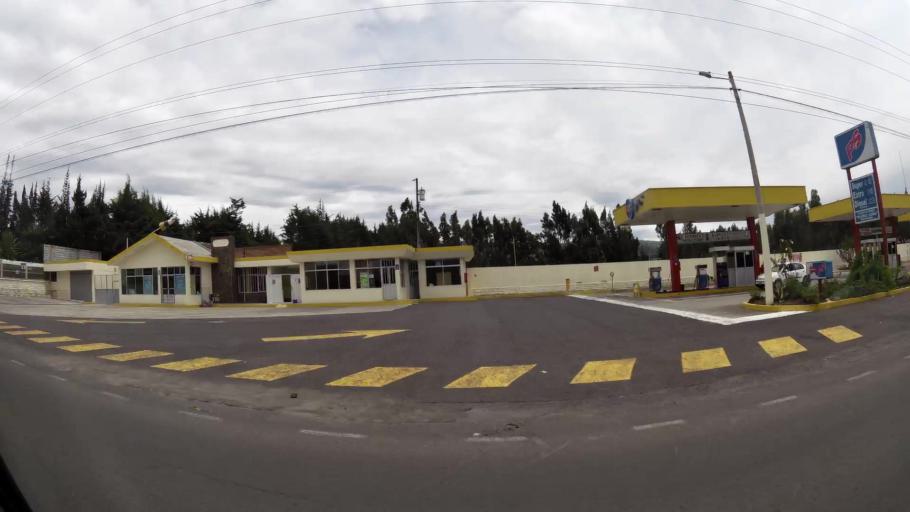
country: EC
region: Cotopaxi
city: San Miguel de Salcedo
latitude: -1.0087
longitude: -78.5932
